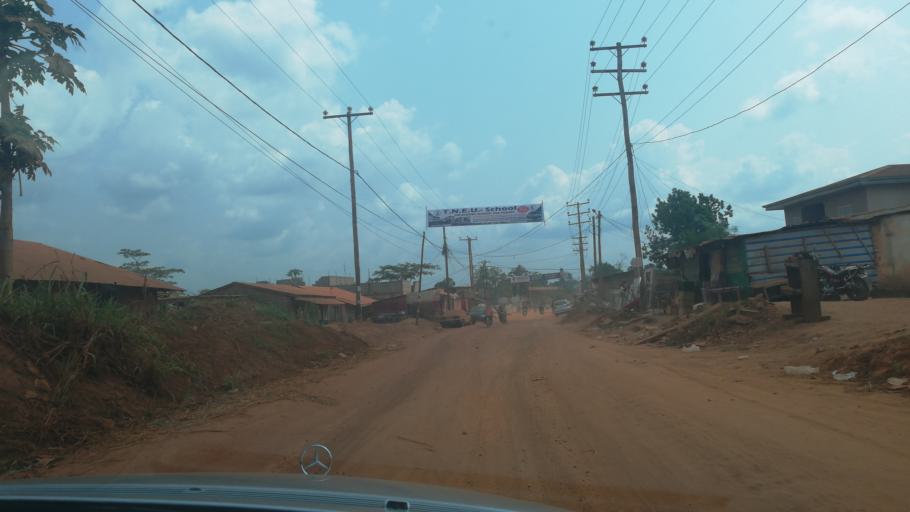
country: CM
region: Centre
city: Yaounde
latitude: 3.7848
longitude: 11.4907
